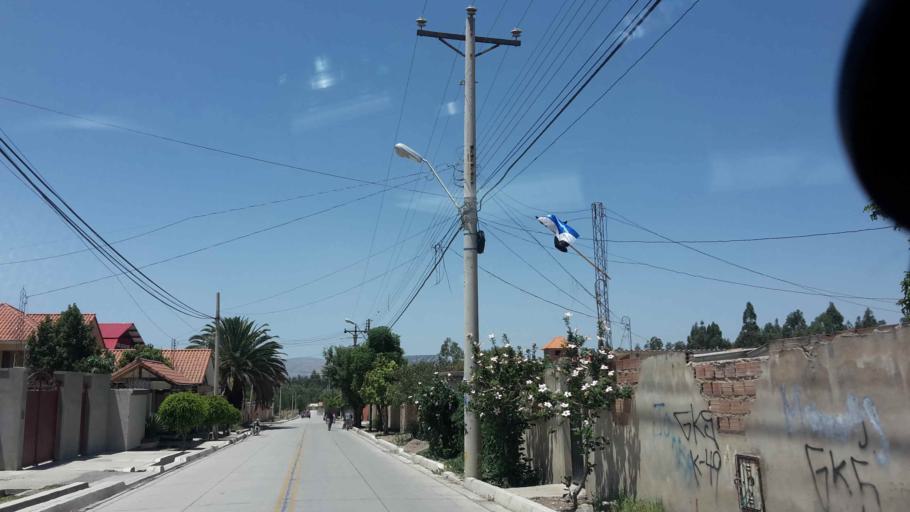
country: BO
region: Cochabamba
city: Cochabamba
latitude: -17.3520
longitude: -66.2065
